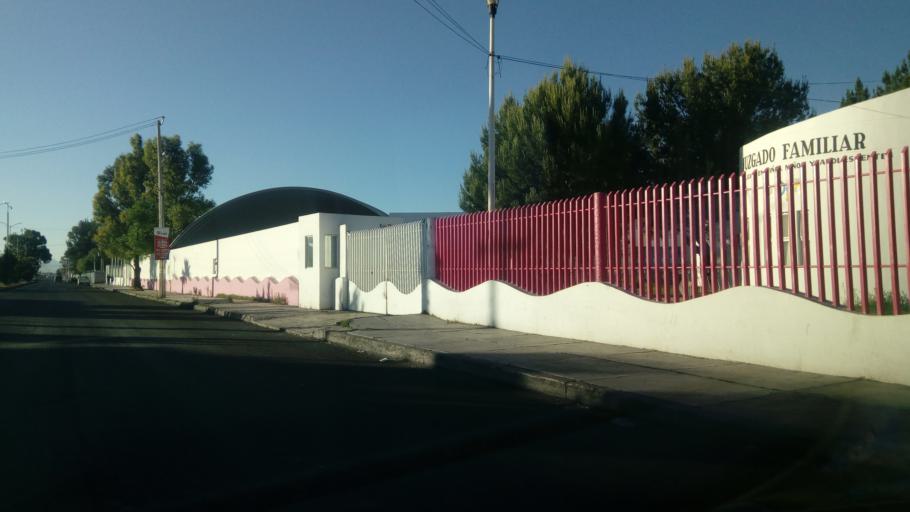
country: MX
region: Durango
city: Victoria de Durango
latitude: 24.0637
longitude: -104.5974
